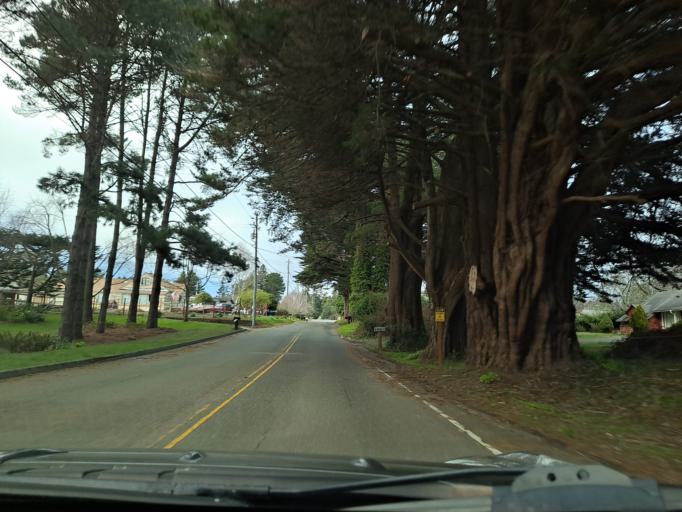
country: US
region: California
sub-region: Humboldt County
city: Fortuna
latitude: 40.6077
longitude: -124.1615
